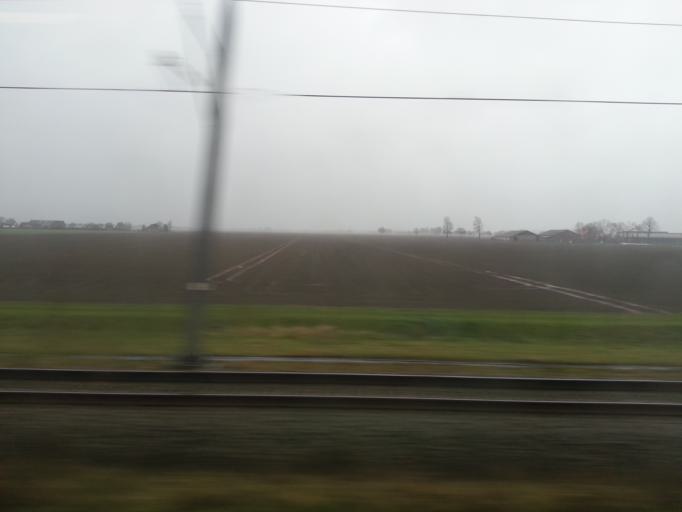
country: NL
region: North Brabant
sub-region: Gemeente Made en Drimmelen
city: Made
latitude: 51.6511
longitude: 4.6896
